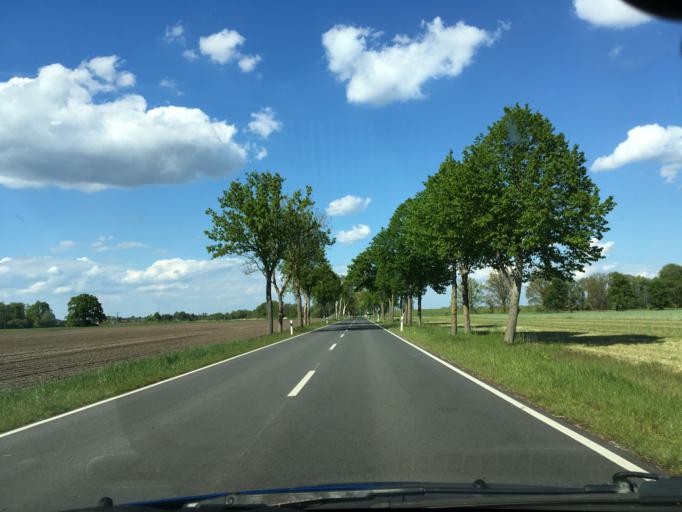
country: DE
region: Brandenburg
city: Lanz
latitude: 53.0219
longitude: 11.5565
